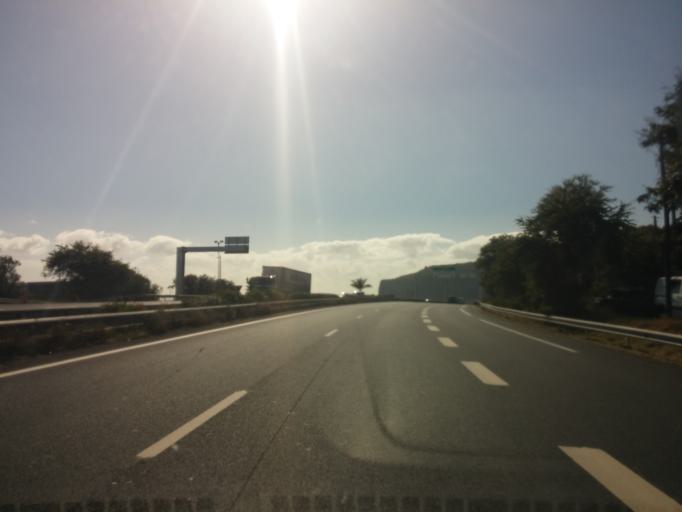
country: RE
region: Reunion
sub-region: Reunion
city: La Possession
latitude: -20.9275
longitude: 55.3329
